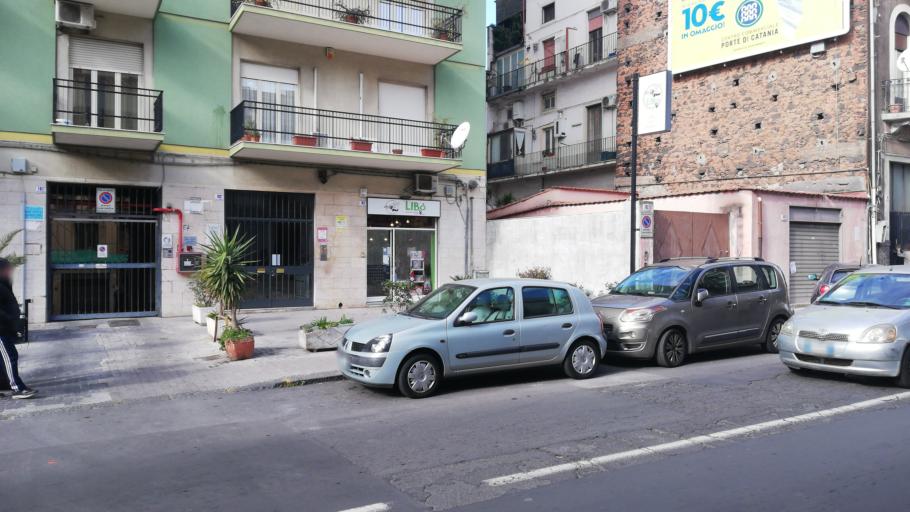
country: IT
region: Sicily
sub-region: Catania
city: Canalicchio
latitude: 37.5189
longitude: 15.0877
